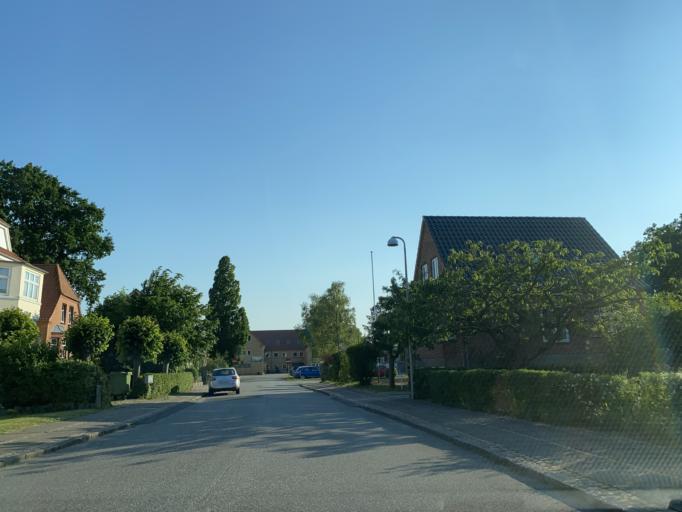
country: DK
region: South Denmark
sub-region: Aabenraa Kommune
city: Aabenraa
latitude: 55.0467
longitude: 9.4117
